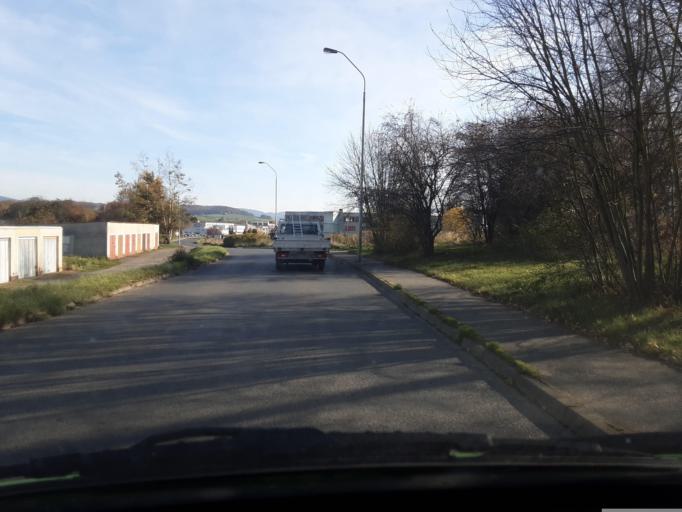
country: CZ
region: Plzensky
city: Klatovy
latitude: 49.3873
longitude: 13.2913
